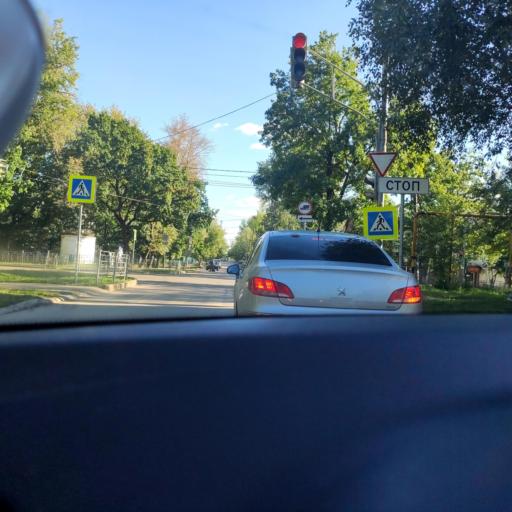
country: RU
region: Samara
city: Volzhskiy
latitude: 53.3474
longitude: 50.2134
